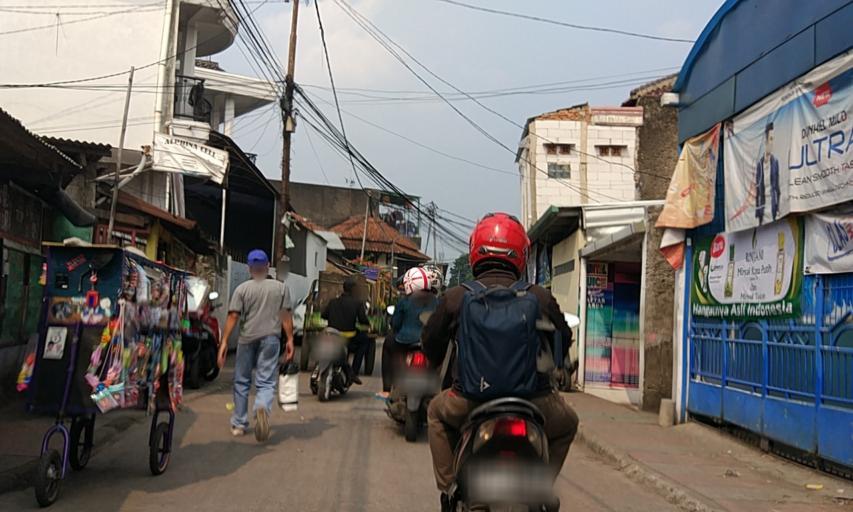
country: ID
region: West Java
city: Bandung
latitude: -6.9117
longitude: 107.6460
